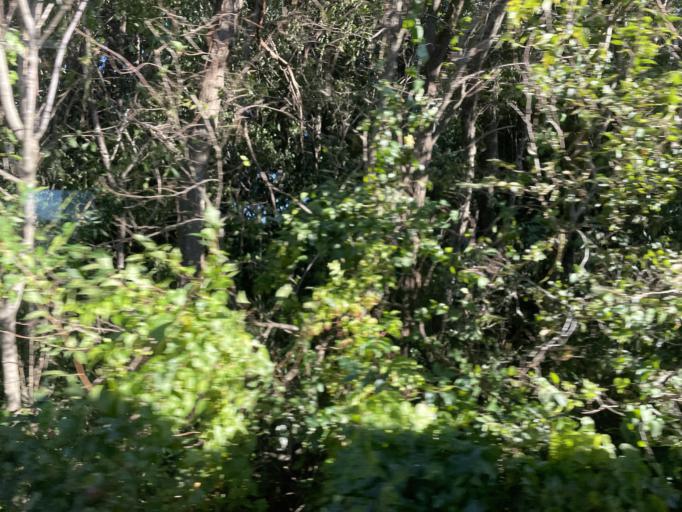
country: JP
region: Tochigi
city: Fujioka
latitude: 36.3073
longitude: 139.6758
